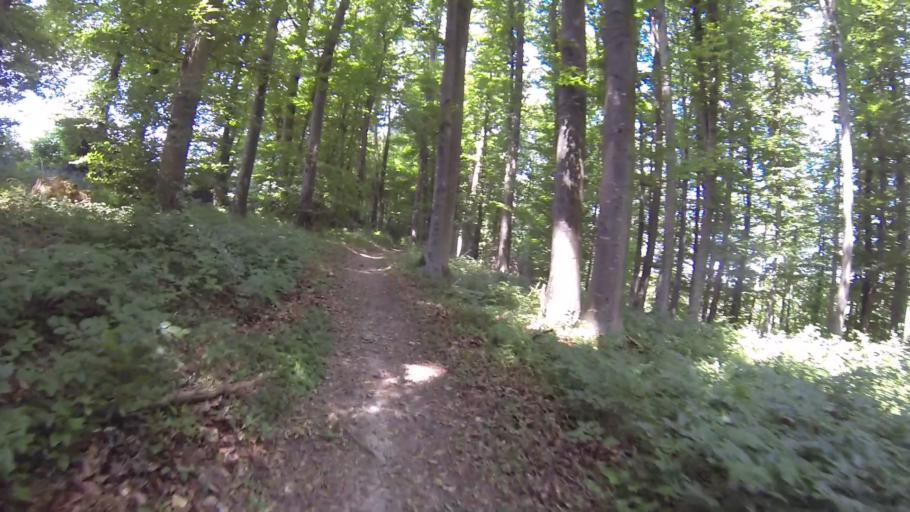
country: DE
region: Baden-Wuerttemberg
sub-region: Regierungsbezirk Stuttgart
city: Bolheim
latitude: 48.6086
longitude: 10.1557
